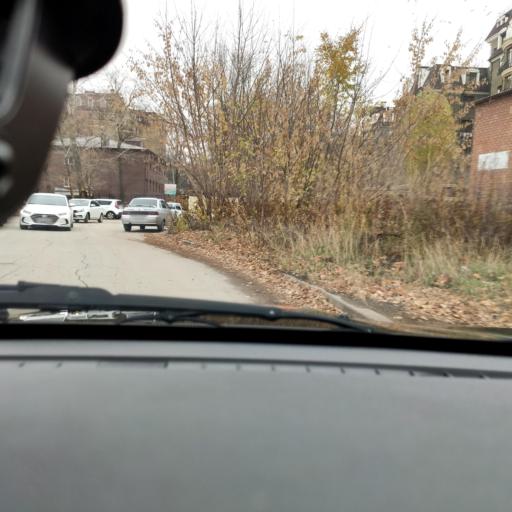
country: RU
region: Samara
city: Tol'yatti
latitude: 53.5375
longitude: 49.3604
